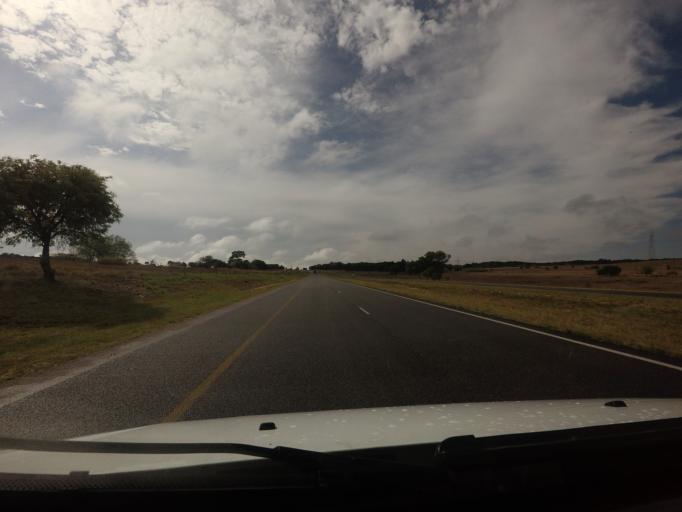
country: ZA
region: Gauteng
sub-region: City of Tshwane Metropolitan Municipality
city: Cullinan
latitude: -25.7933
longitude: 28.4960
